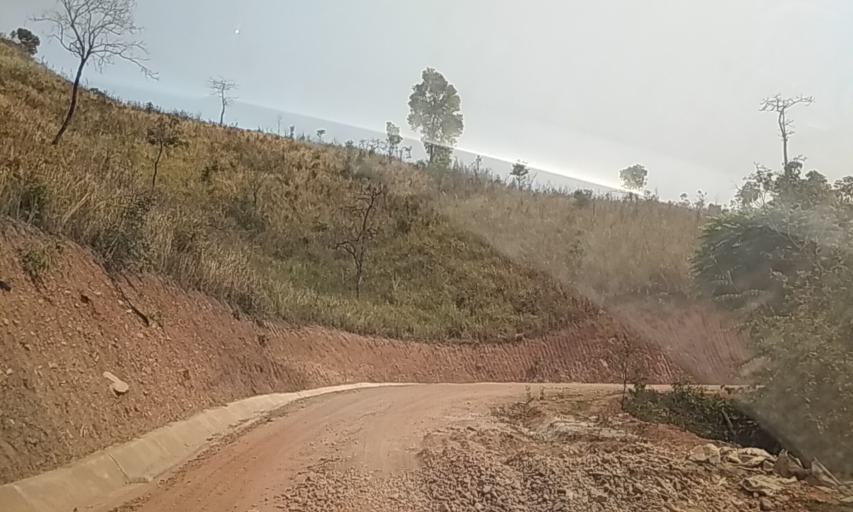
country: VN
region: Huyen Dien Bien
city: Dien Bien Phu
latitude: 21.4945
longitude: 102.7854
